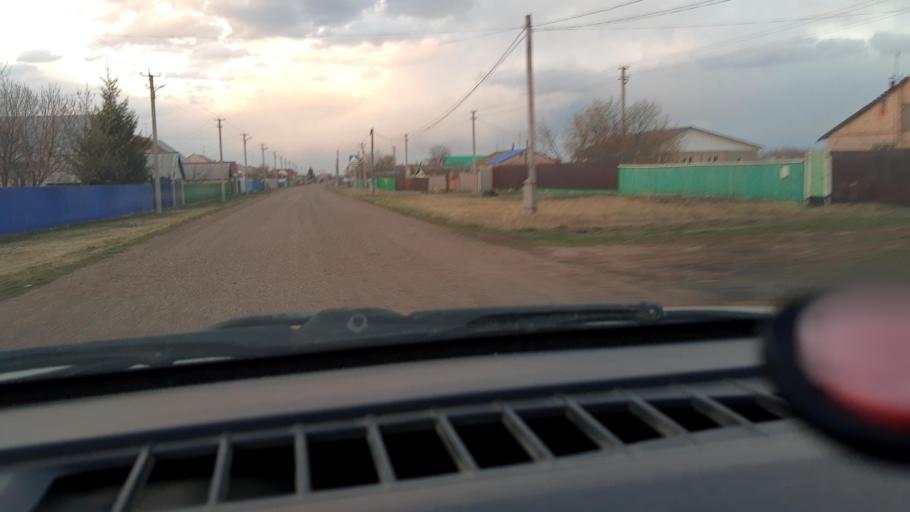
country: RU
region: Bashkortostan
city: Asanovo
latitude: 54.9052
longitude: 55.4854
